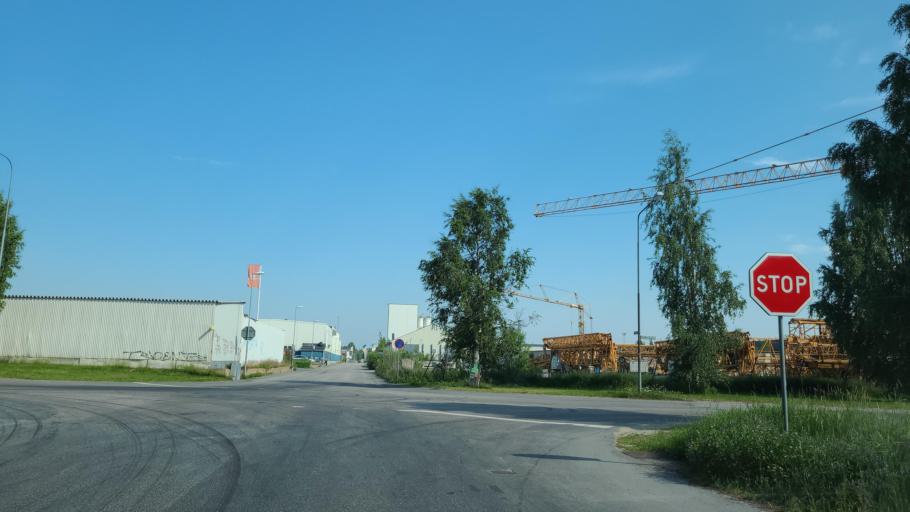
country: SE
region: Vaesterbotten
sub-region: Umea Kommun
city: Umea
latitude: 63.8438
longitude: 20.2254
